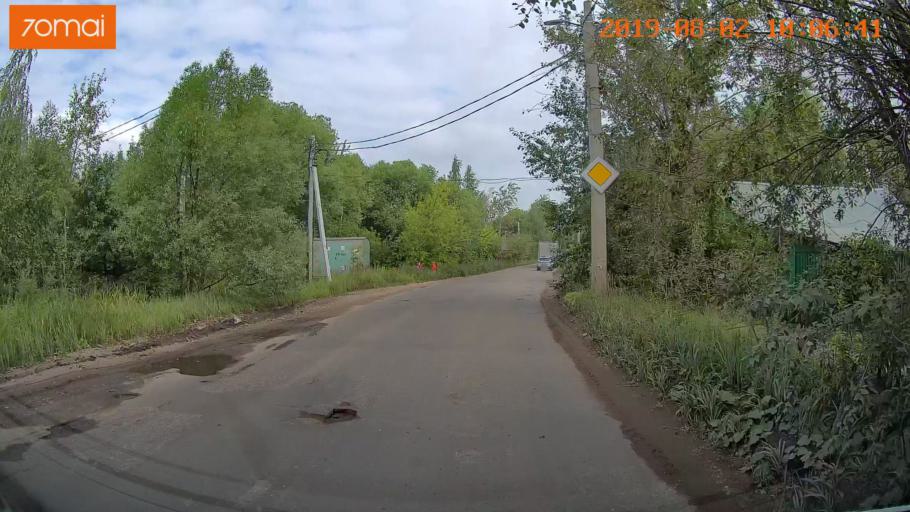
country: RU
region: Ivanovo
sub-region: Gorod Ivanovo
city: Ivanovo
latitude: 56.9801
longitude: 40.9351
